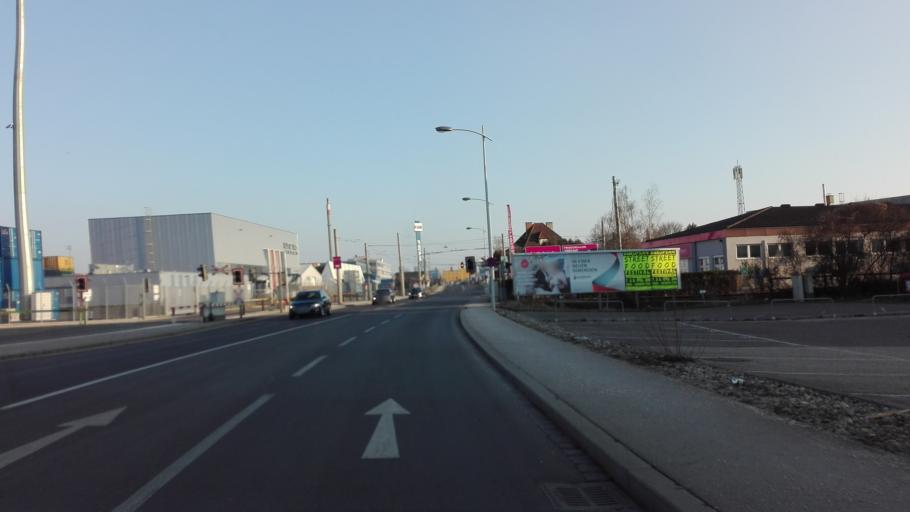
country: AT
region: Upper Austria
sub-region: Linz Stadt
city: Linz
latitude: 48.3113
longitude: 14.3137
